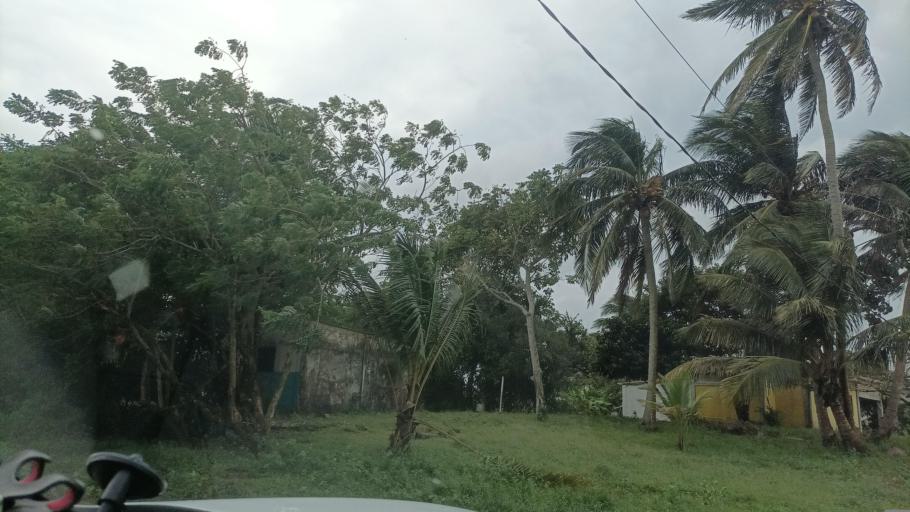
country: MX
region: Veracruz
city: Agua Dulce
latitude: 18.2080
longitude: -94.1431
